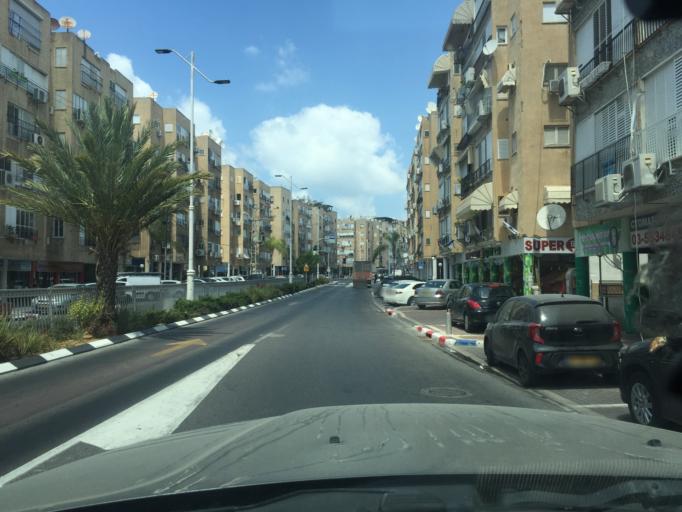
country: IL
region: Tel Aviv
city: Bat Yam
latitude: 32.0127
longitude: 34.7423
